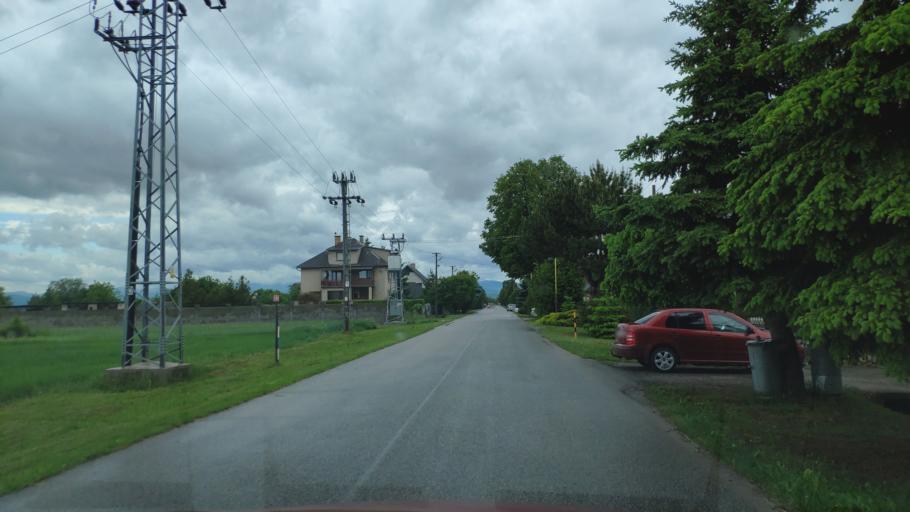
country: SK
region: Kosicky
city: Moldava nad Bodvou
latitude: 48.5330
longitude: 21.1099
